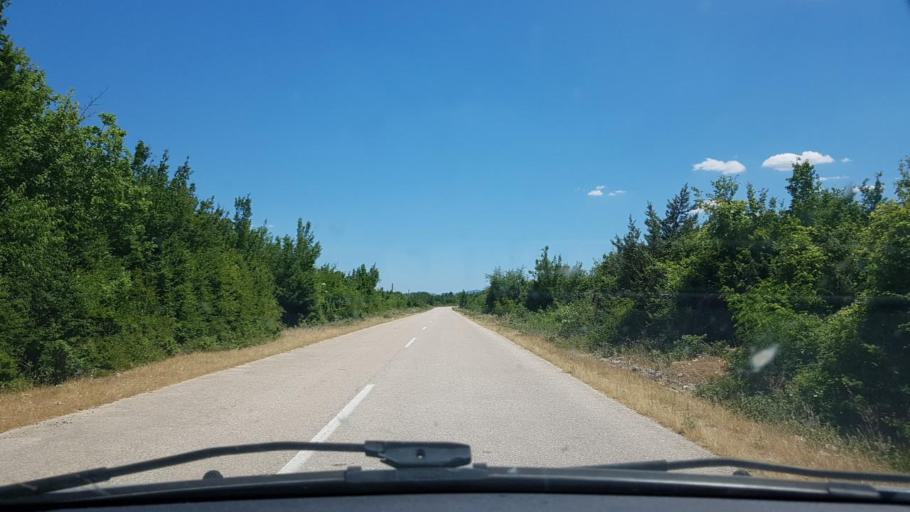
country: HR
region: Sibensko-Kniniska
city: Kistanje
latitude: 43.9694
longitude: 15.9759
